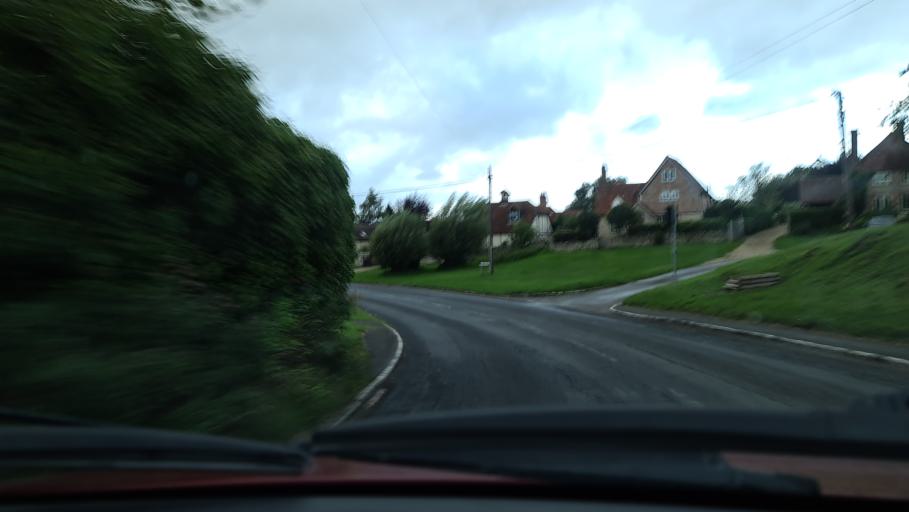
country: GB
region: England
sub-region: Buckinghamshire
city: Long Crendon
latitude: 51.7771
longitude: -1.0049
